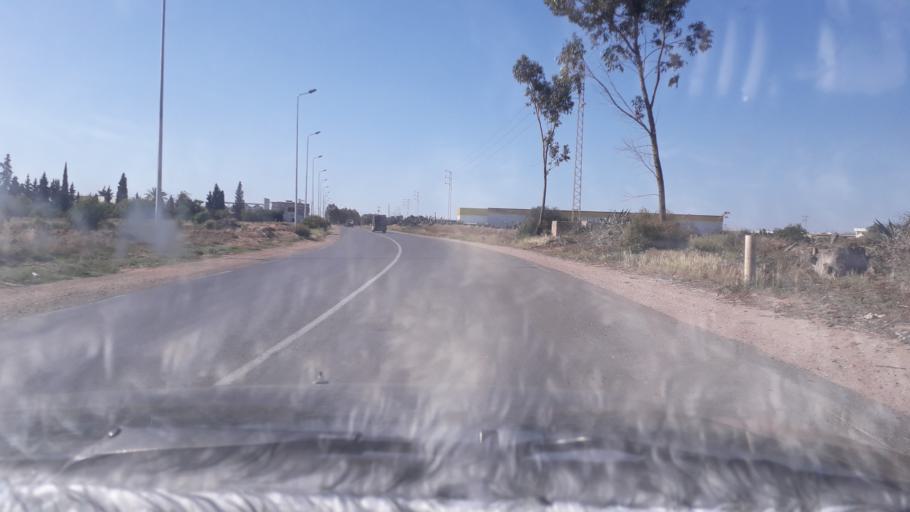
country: TN
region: Safaqis
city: Al Qarmadah
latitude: 34.8719
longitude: 10.7559
